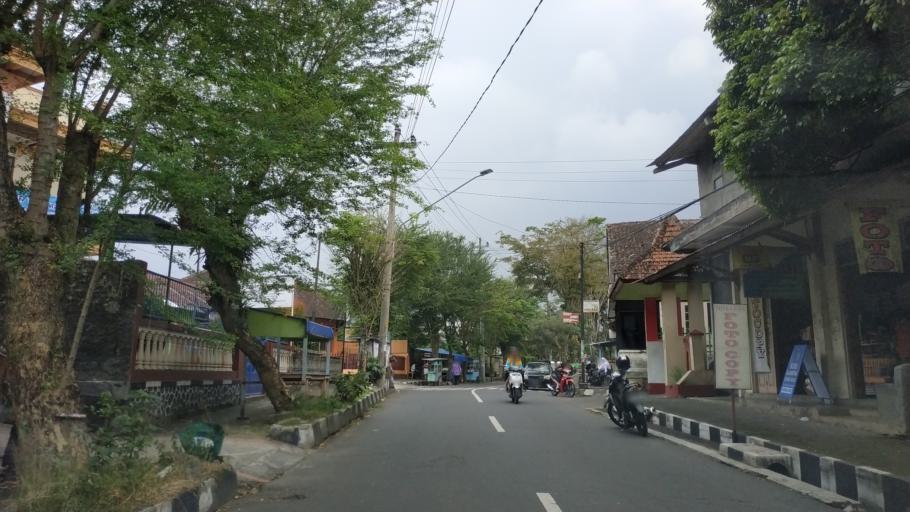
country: ID
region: Central Java
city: Magelang
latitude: -7.3101
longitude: 110.1770
